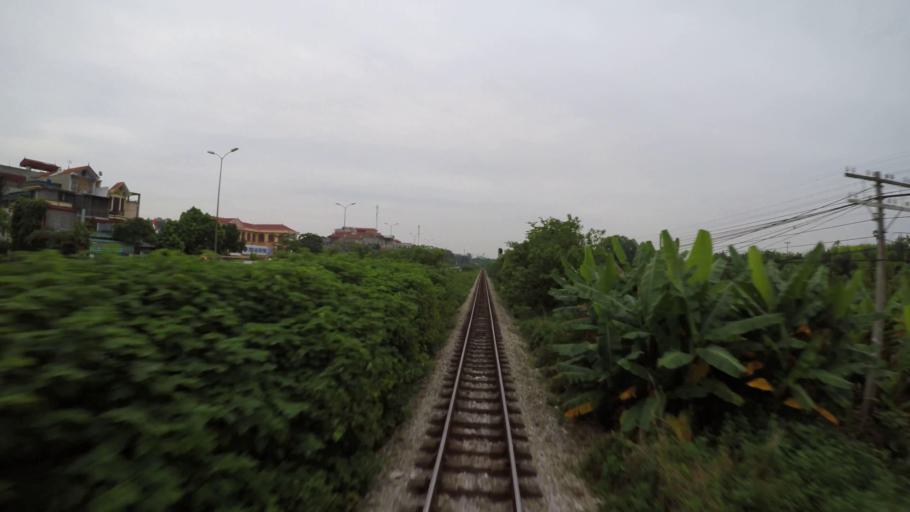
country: VN
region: Ha Noi
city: Trau Quy
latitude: 21.0124
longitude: 105.9501
